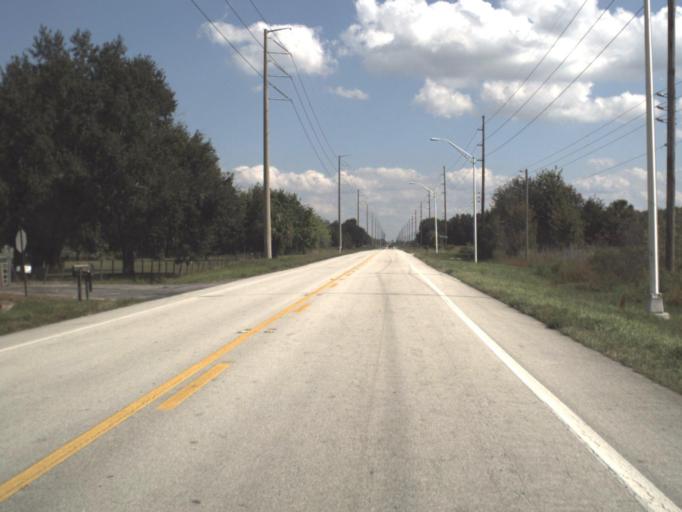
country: US
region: Florida
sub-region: Highlands County
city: Sebring
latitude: 27.4124
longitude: -81.5072
